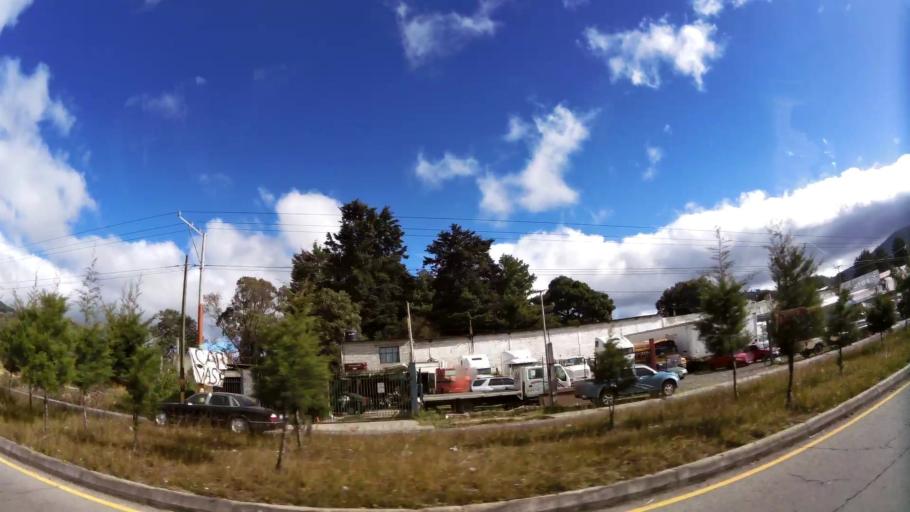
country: GT
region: Quetzaltenango
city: Salcaja
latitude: 14.8945
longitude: -91.4570
